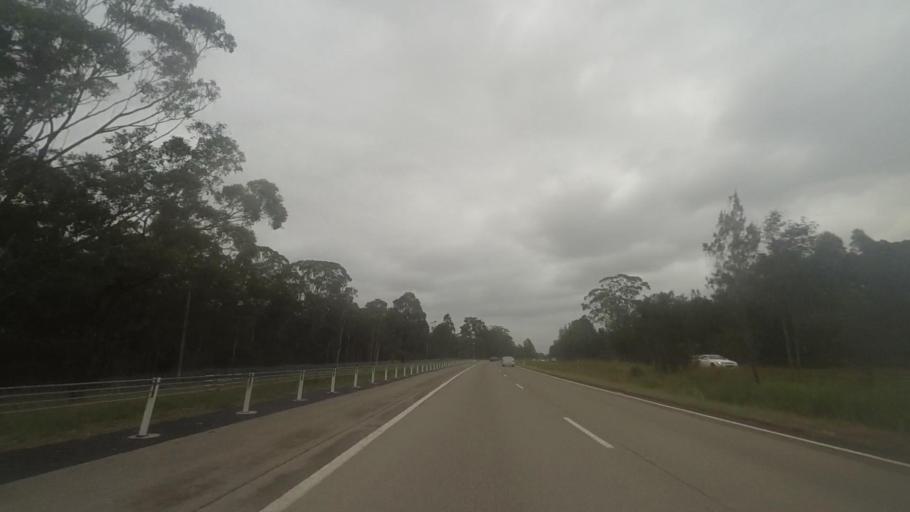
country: AU
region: New South Wales
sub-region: Port Stephens Shire
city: Raymond Terrace
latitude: -32.7088
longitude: 151.7983
